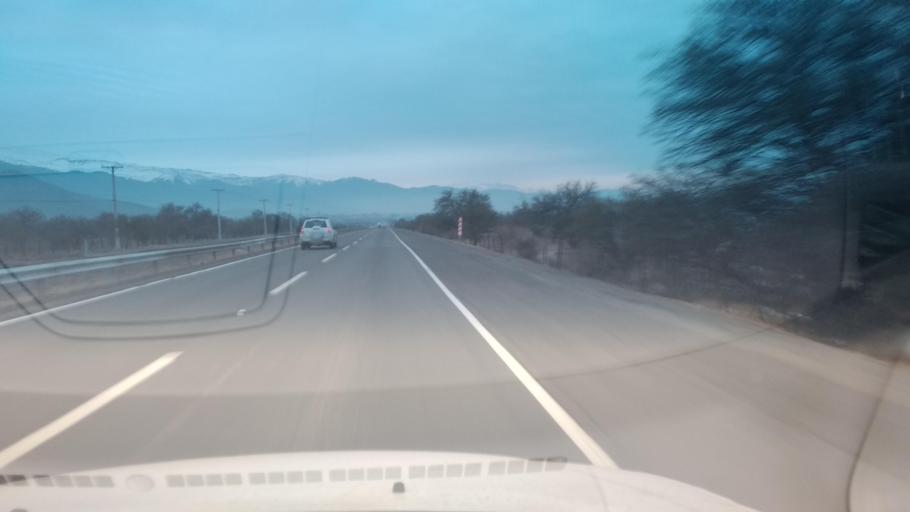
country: CL
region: Santiago Metropolitan
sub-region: Provincia de Chacabuco
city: Chicureo Abajo
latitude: -33.1123
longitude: -70.6862
